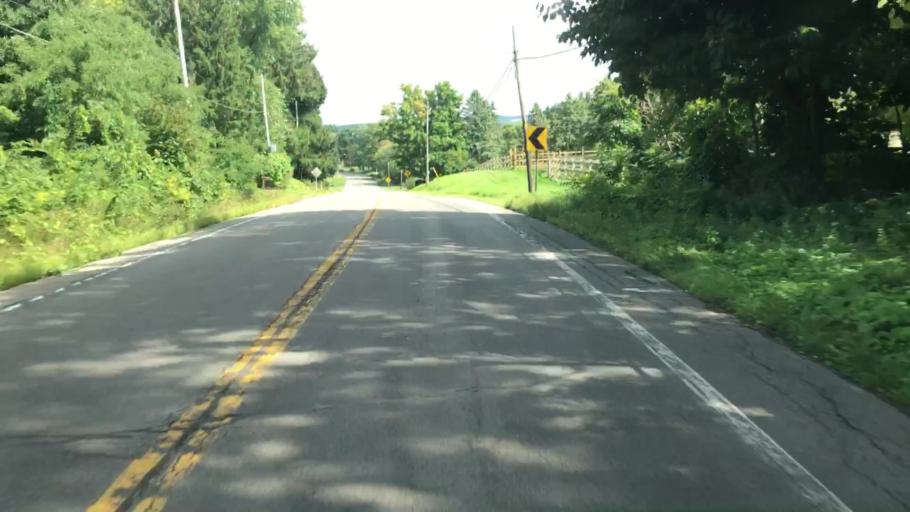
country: US
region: New York
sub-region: Onondaga County
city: Marcellus
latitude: 42.9832
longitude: -76.2792
